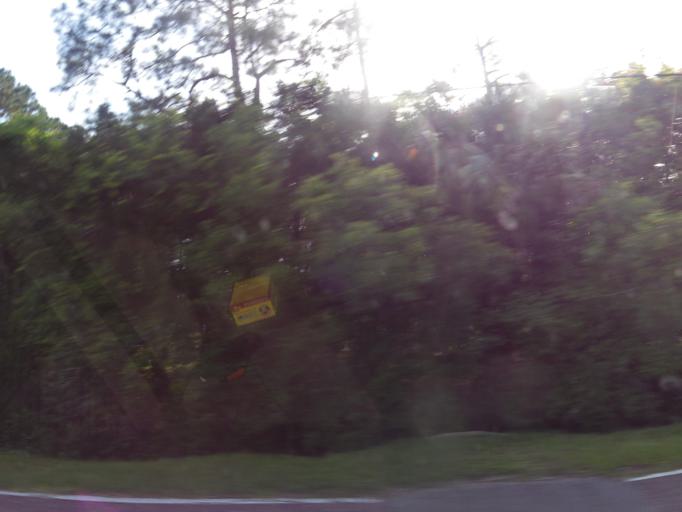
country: US
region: Florida
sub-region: Nassau County
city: Fernandina Beach
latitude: 30.5236
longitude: -81.4819
